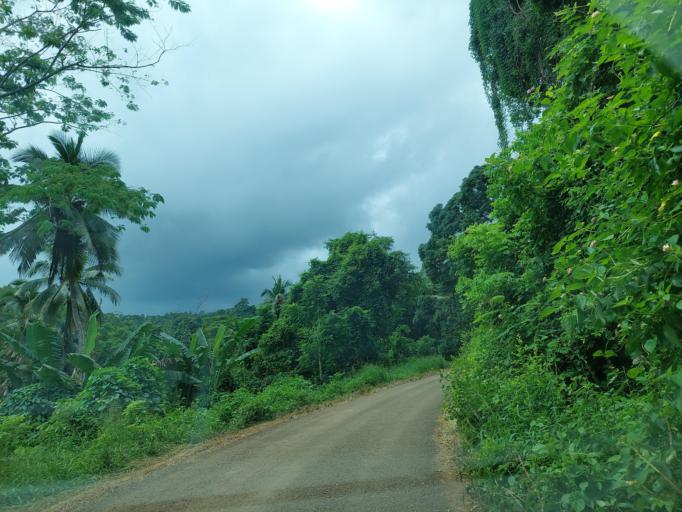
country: YT
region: Tsingoni
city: Tsingoni
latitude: -12.7732
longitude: 45.1109
